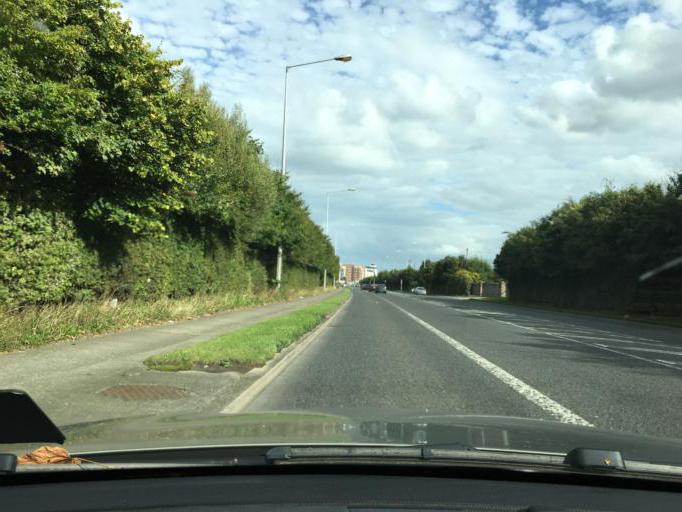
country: IE
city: Darndale
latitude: 53.4051
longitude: -6.1910
